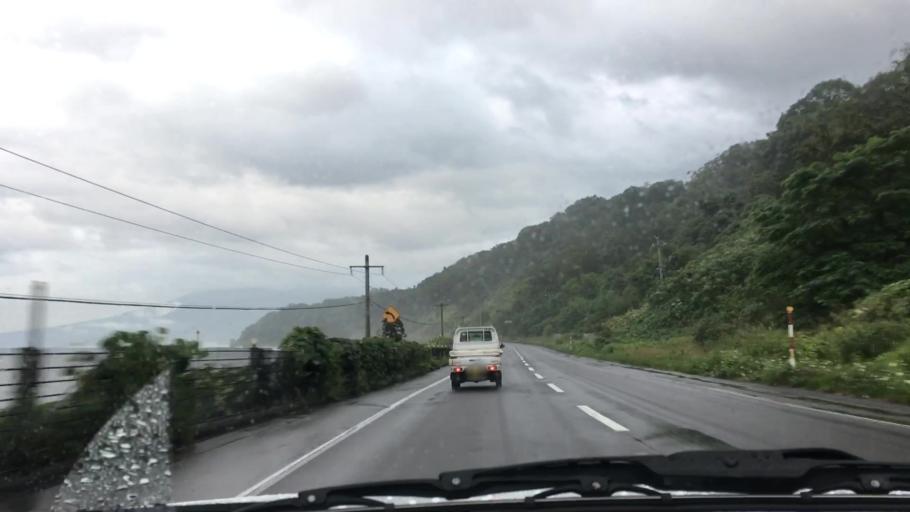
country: JP
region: Hokkaido
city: Nanae
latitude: 42.1271
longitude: 140.5173
